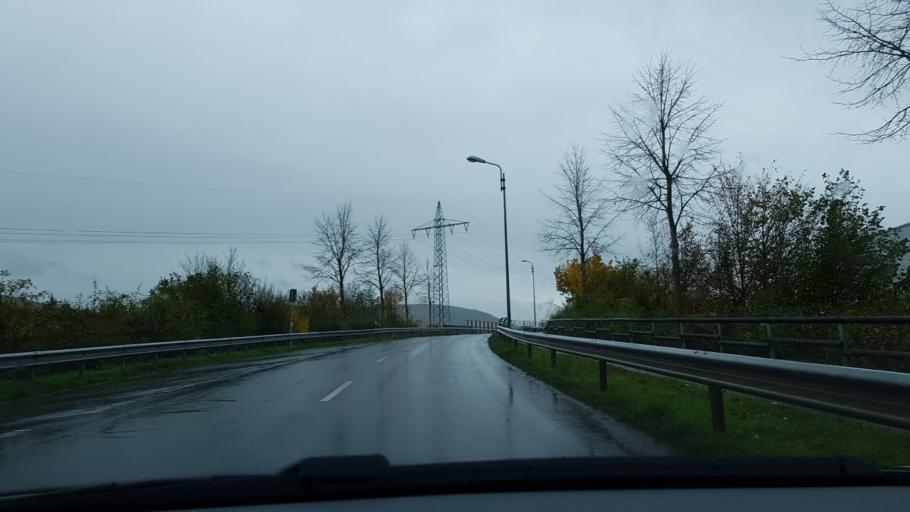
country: DE
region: Rheinland-Pfalz
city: Neuerburg
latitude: 49.9770
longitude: 6.9556
